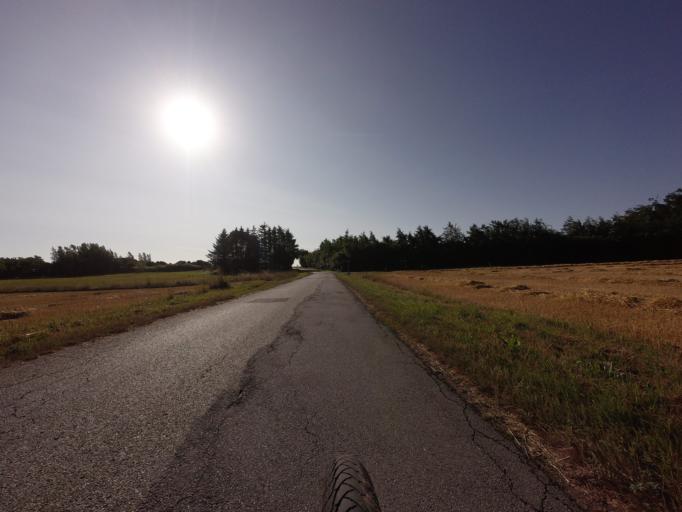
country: DK
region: North Denmark
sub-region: Hjorring Kommune
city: Vra
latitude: 57.3777
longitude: 9.9768
